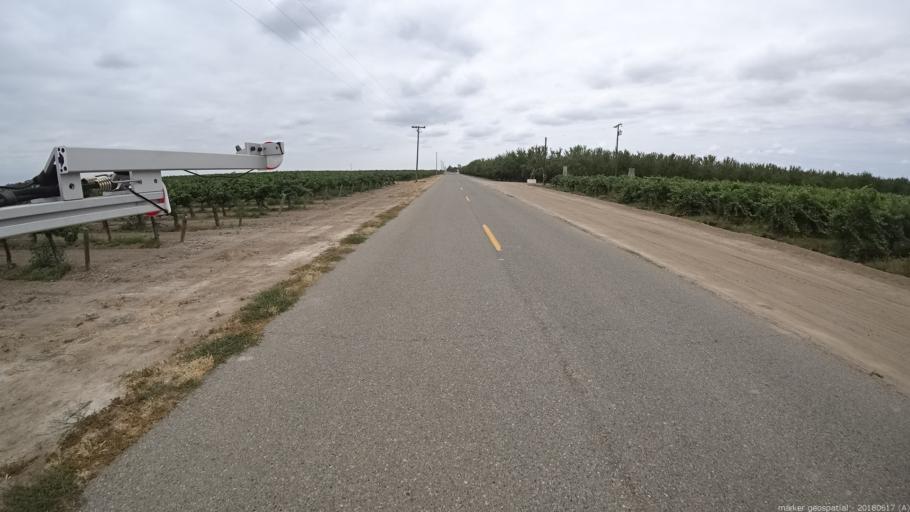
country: US
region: California
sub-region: Madera County
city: Madera
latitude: 36.9279
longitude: -120.1560
